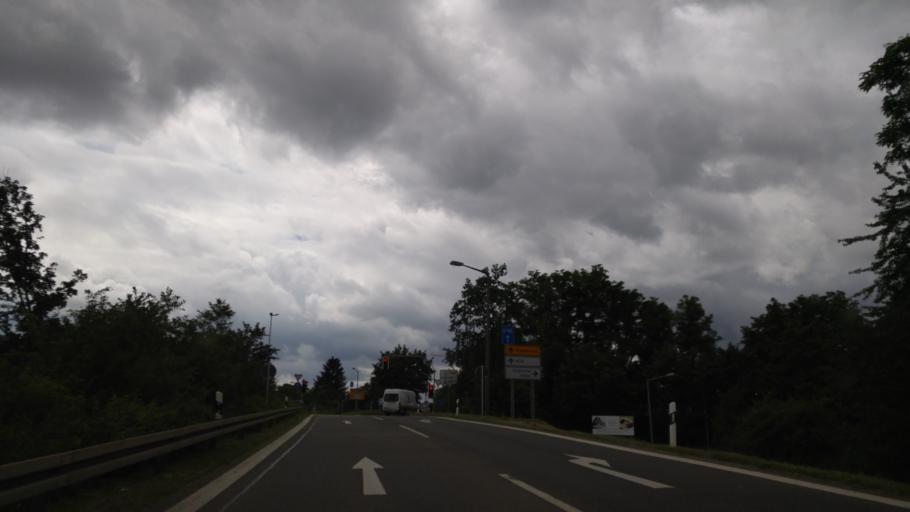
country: DE
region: Bavaria
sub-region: Regierungsbezirk Mittelfranken
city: Furth
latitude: 49.4825
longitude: 11.0044
